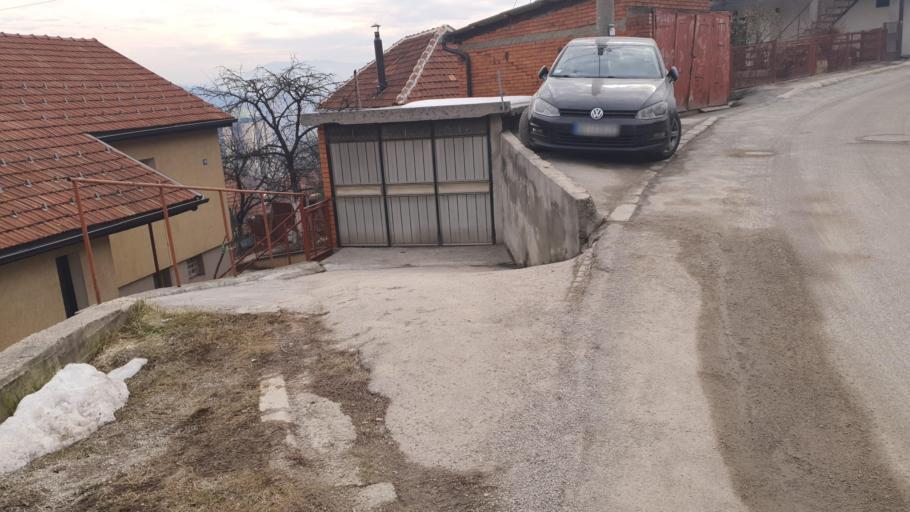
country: RS
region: Central Serbia
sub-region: Zlatiborski Okrug
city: Uzice
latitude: 43.8606
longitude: 19.8357
